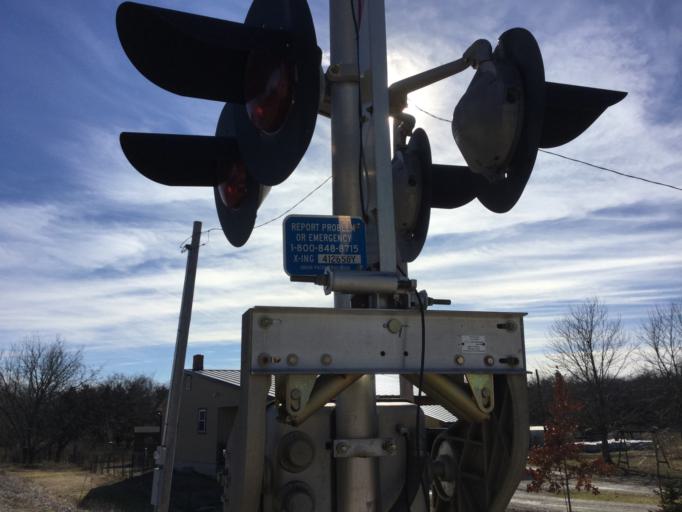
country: US
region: Kansas
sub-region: Allen County
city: Iola
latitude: 37.9942
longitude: -95.1639
